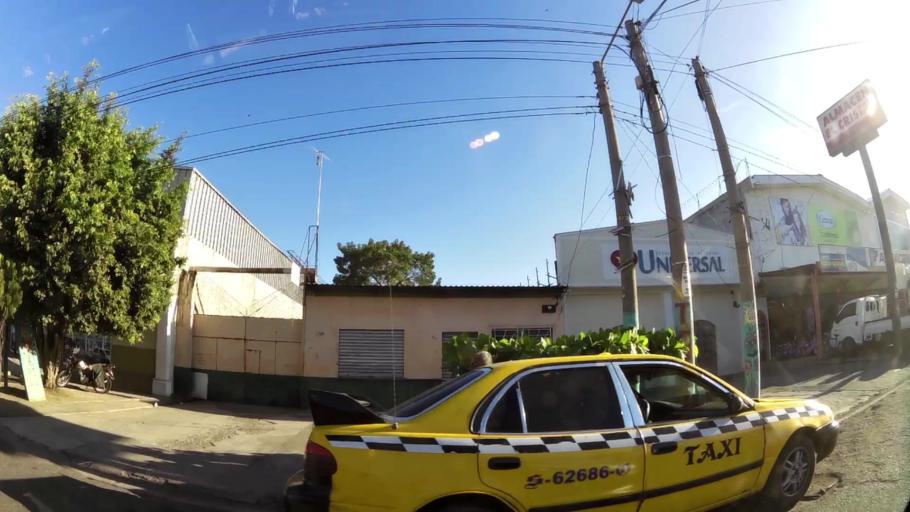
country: SV
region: Sonsonate
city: Sonsonate
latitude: 13.7170
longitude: -89.7226
